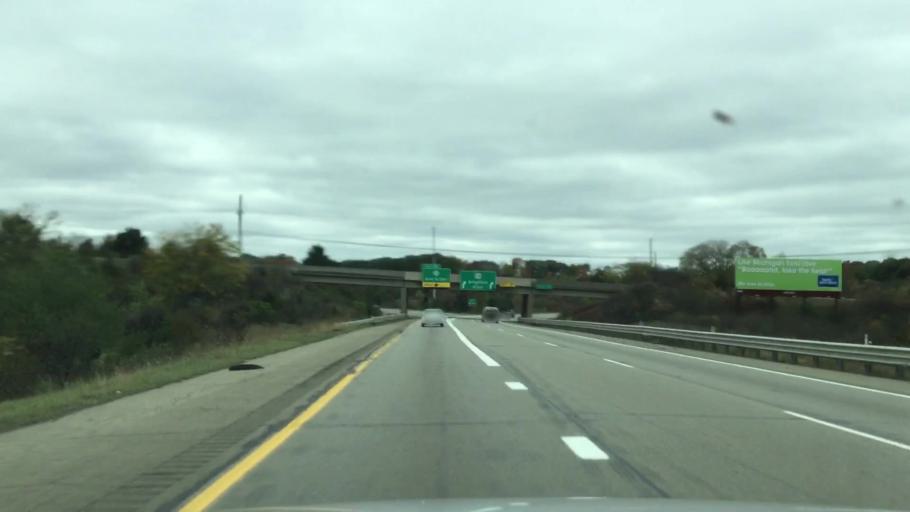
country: US
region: Michigan
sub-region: Washtenaw County
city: Ann Arbor
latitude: 42.3217
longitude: -83.7342
